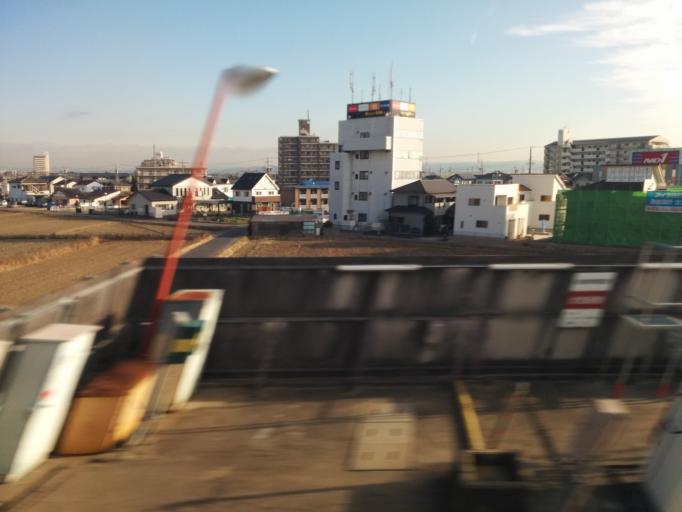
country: JP
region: Aichi
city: Anjo
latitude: 34.9386
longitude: 137.0884
